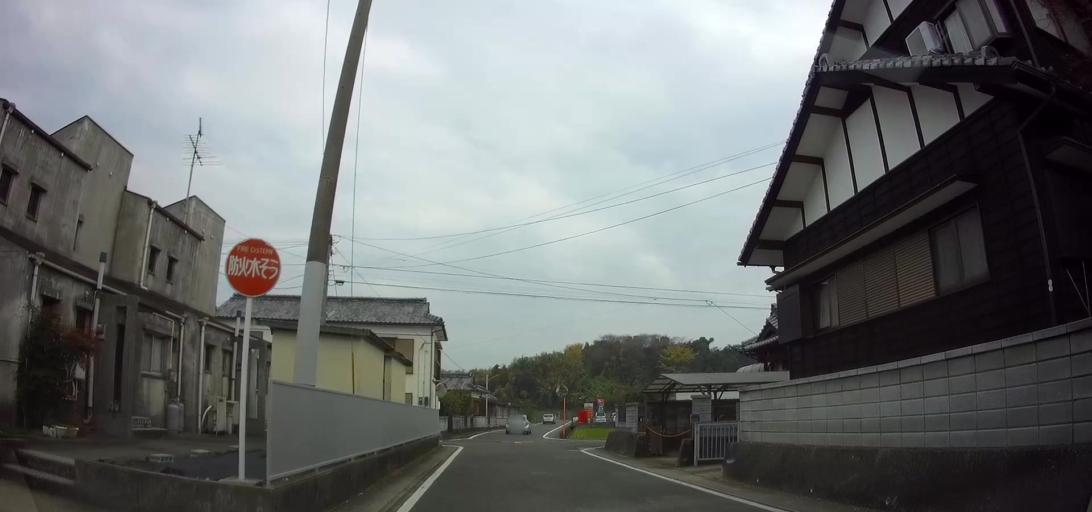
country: JP
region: Nagasaki
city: Shimabara
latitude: 32.6670
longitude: 130.3008
